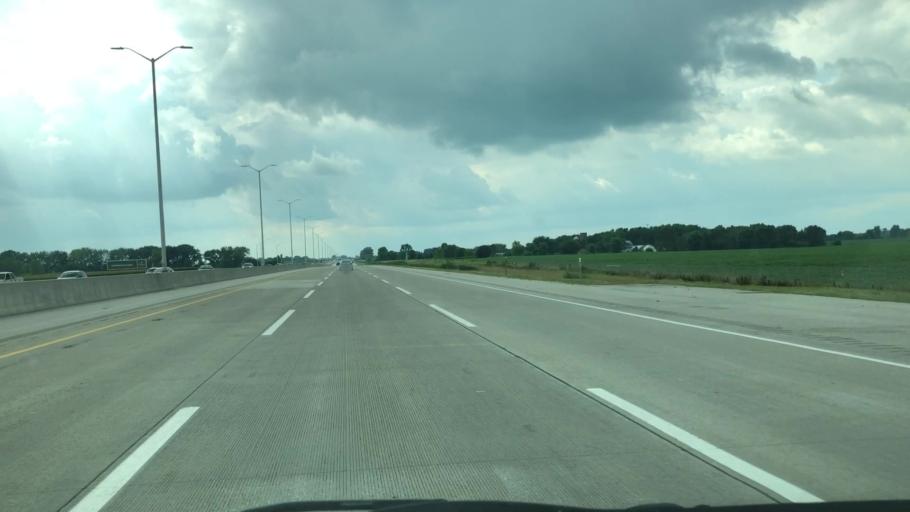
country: US
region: Illinois
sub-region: DeKalb County
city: Kingston
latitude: 42.2136
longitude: -88.7303
